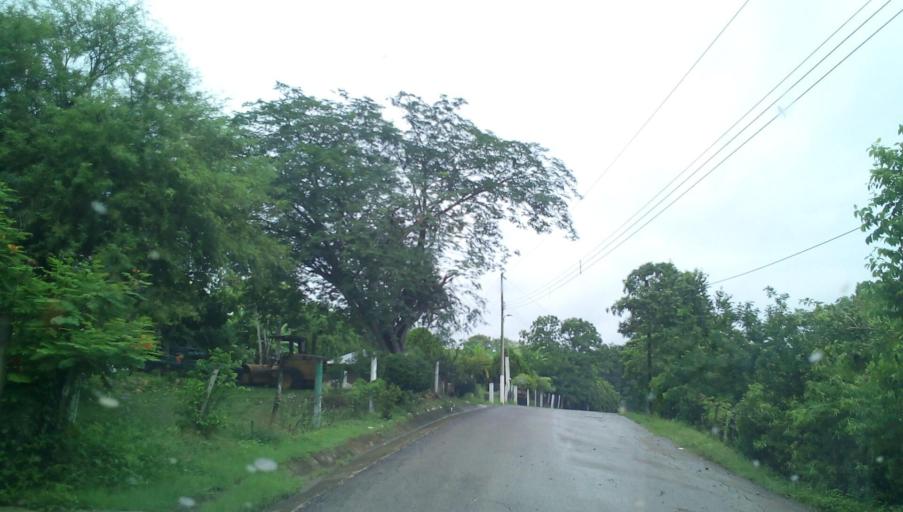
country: MX
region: Veracruz
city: Tempoal de Sanchez
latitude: 21.4601
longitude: -98.4268
